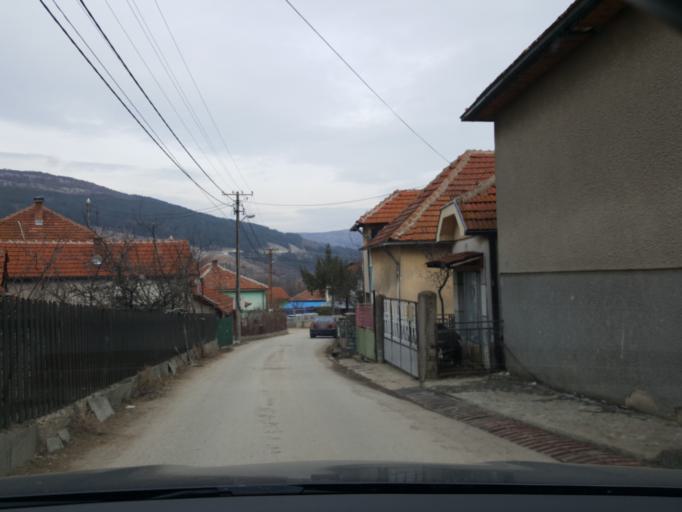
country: RS
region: Central Serbia
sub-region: Pirotski Okrug
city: Dimitrovgrad
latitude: 43.0085
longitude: 22.7517
